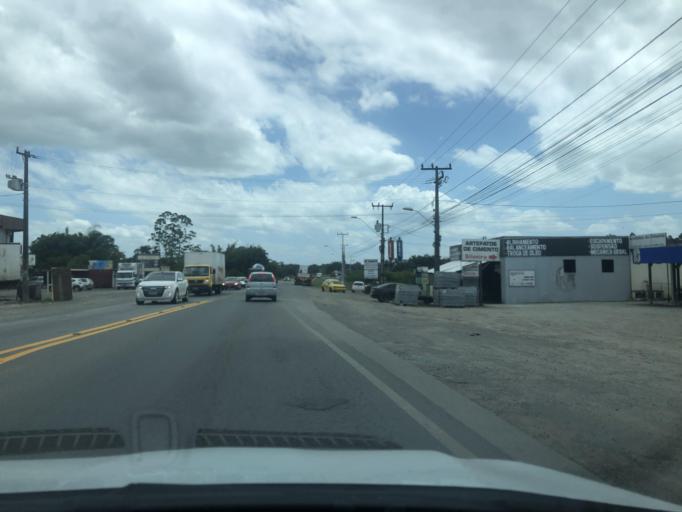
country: BR
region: Santa Catarina
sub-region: Joinville
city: Joinville
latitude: -26.4101
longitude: -48.7523
